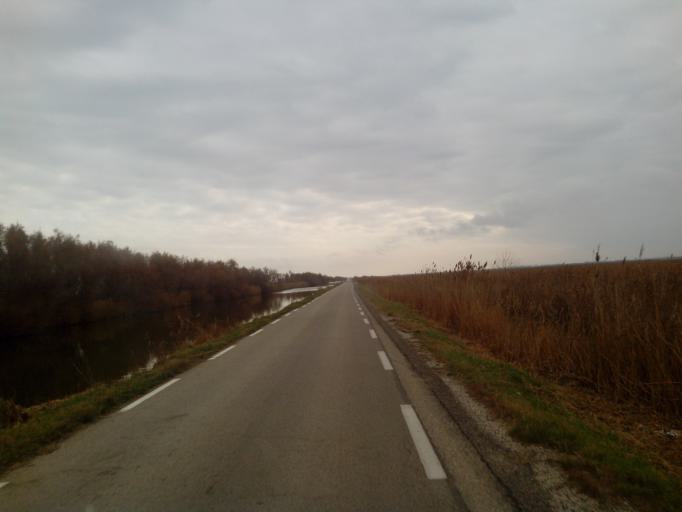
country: FR
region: Languedoc-Roussillon
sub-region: Departement du Gard
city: Vauvert
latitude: 43.6338
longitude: 4.3029
